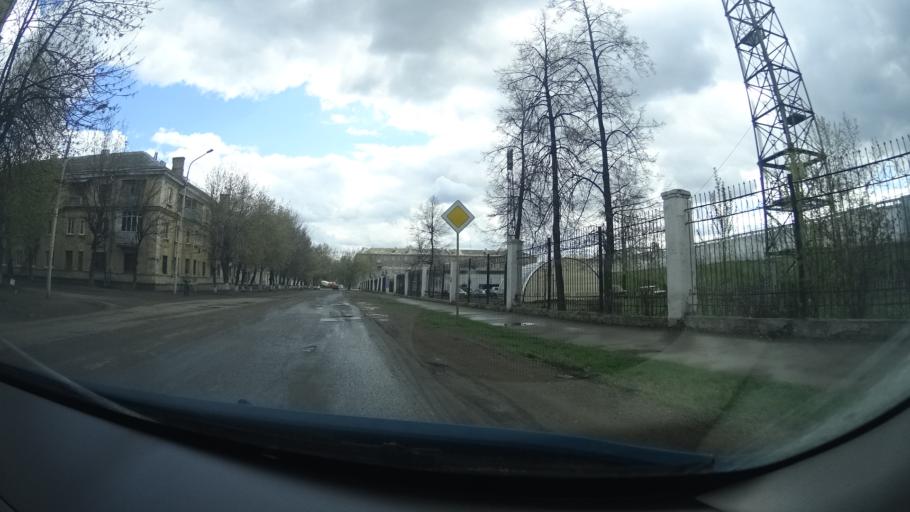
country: RU
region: Bashkortostan
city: Ufa
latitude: 54.8181
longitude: 56.0963
